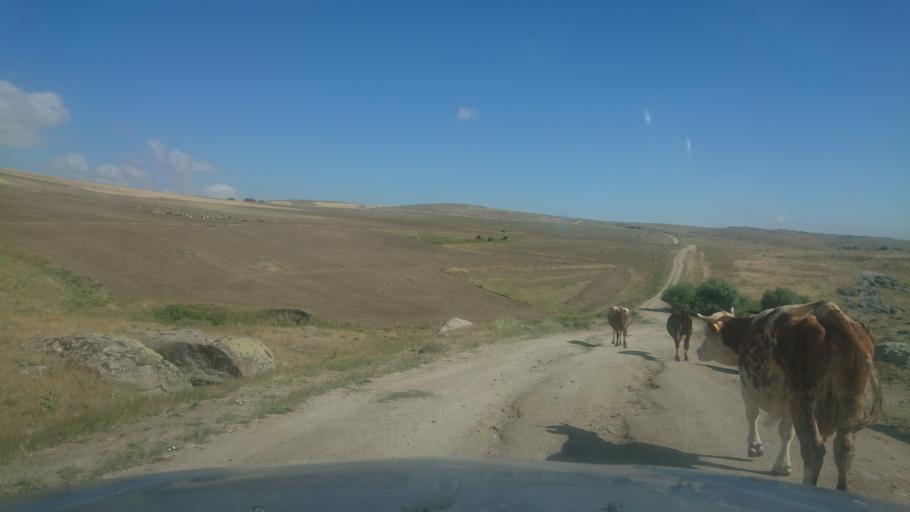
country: TR
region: Aksaray
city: Agacoren
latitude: 38.9123
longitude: 33.8554
